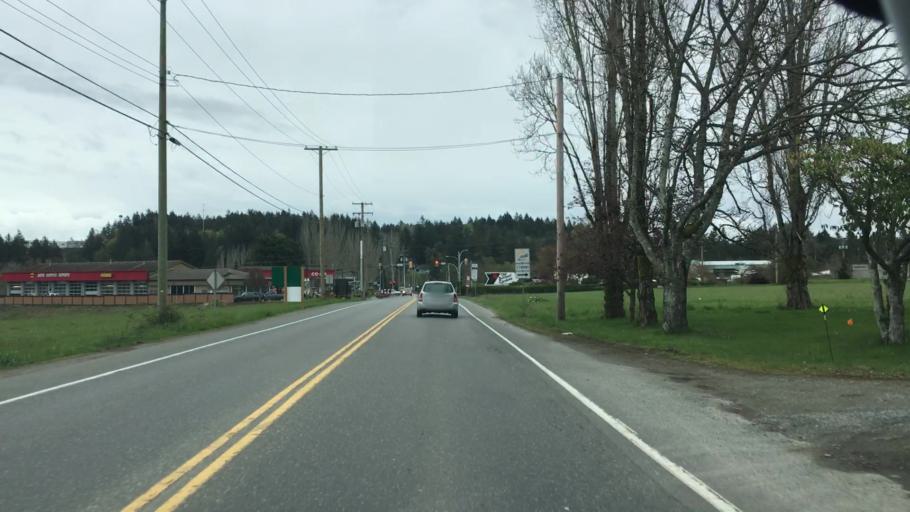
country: CA
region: British Columbia
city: North Saanich
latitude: 48.5667
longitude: -123.4399
